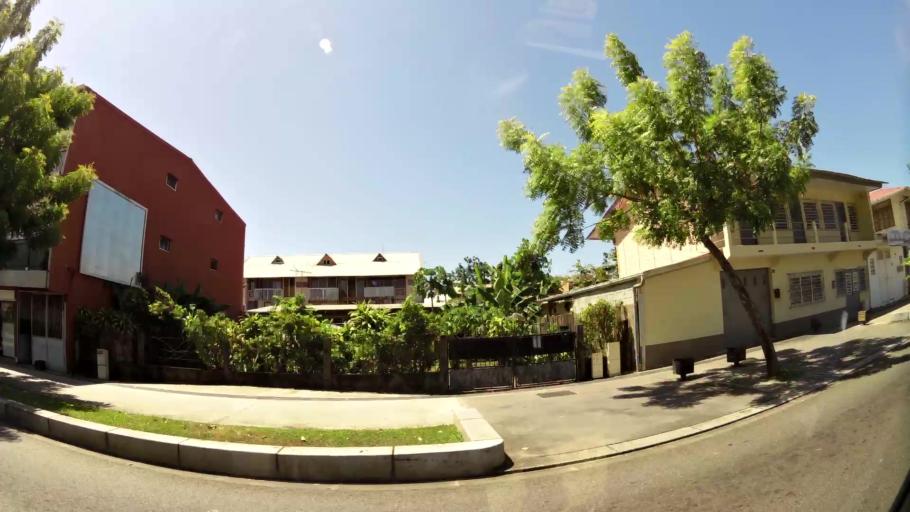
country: GF
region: Guyane
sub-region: Guyane
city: Cayenne
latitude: 4.9404
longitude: -52.3254
